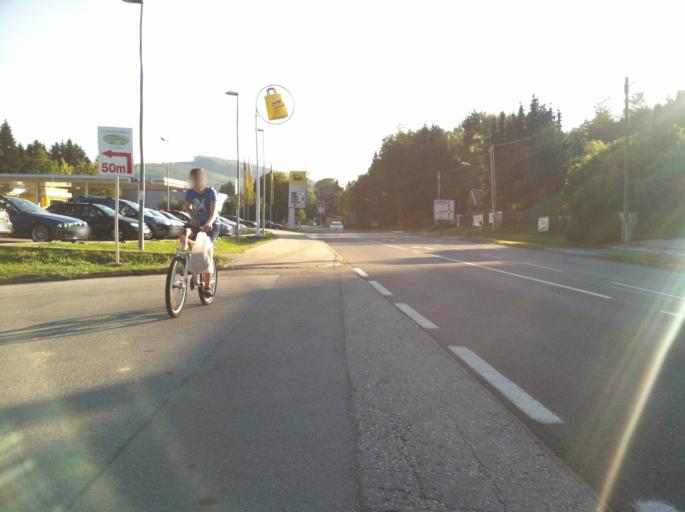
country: AT
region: Lower Austria
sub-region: Politischer Bezirk Wien-Umgebung
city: Wolfsgraben
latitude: 48.1875
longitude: 16.1247
